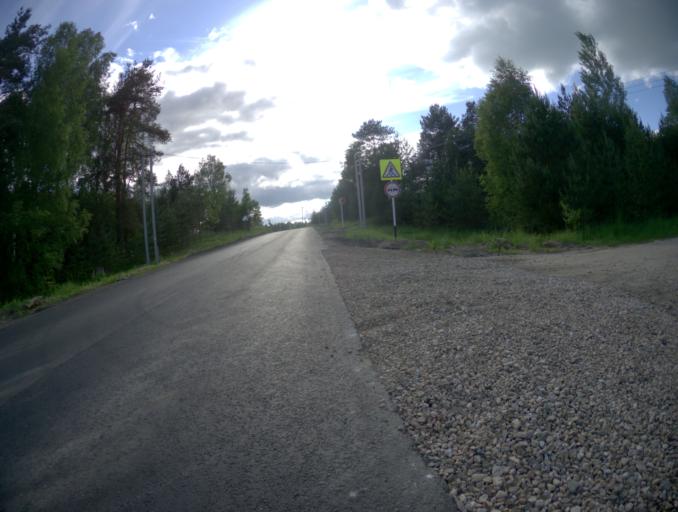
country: RU
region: Ivanovo
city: Novyye Gorki
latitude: 56.8138
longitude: 41.0689
